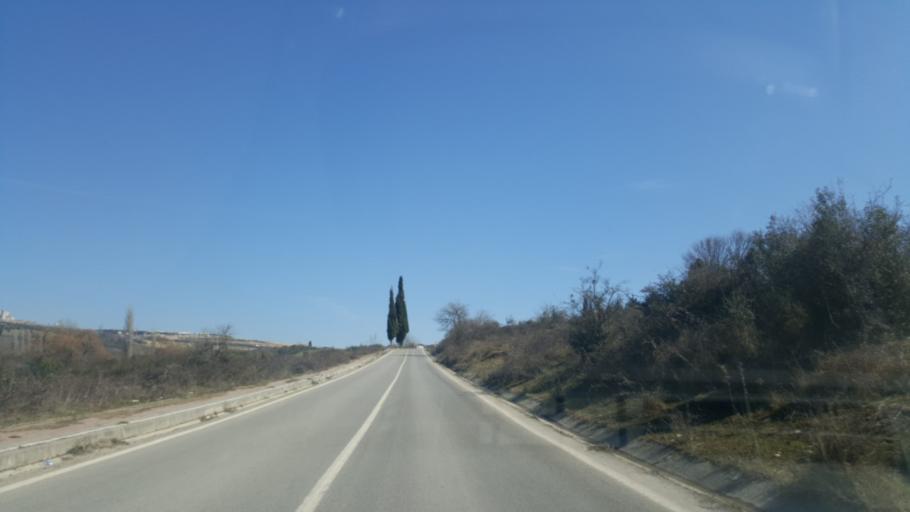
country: TR
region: Kocaeli
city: Tavsancil
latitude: 40.7889
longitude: 29.5687
